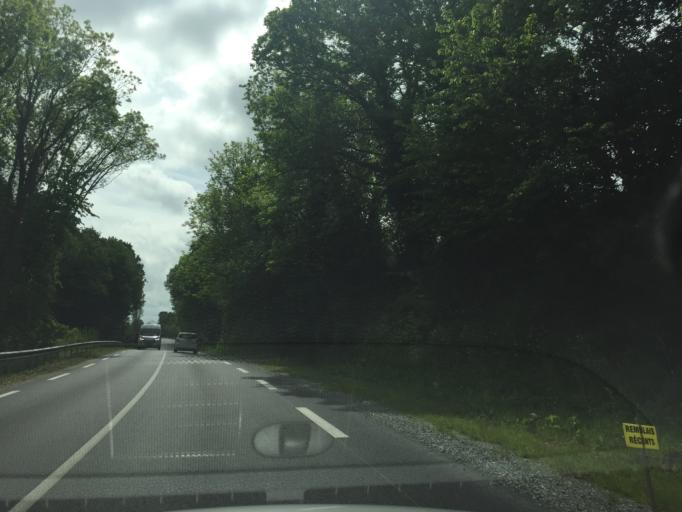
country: FR
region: Brittany
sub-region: Departement des Cotes-d'Armor
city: Crehen
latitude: 48.5689
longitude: -2.2104
